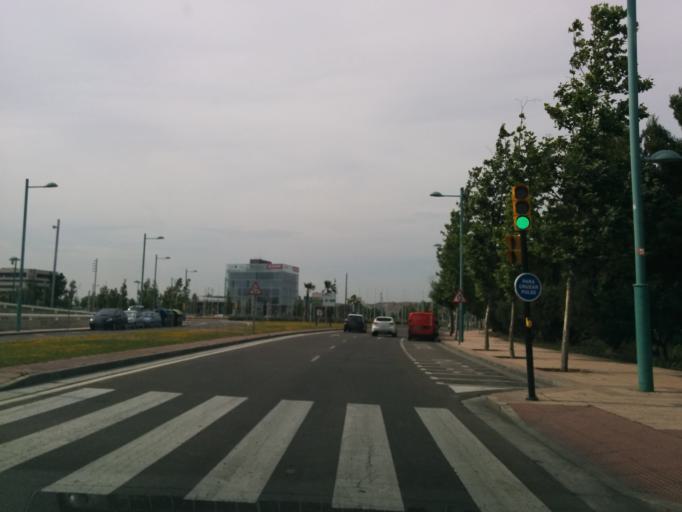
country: ES
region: Aragon
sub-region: Provincia de Zaragoza
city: Almozara
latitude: 41.6700
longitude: -0.8968
